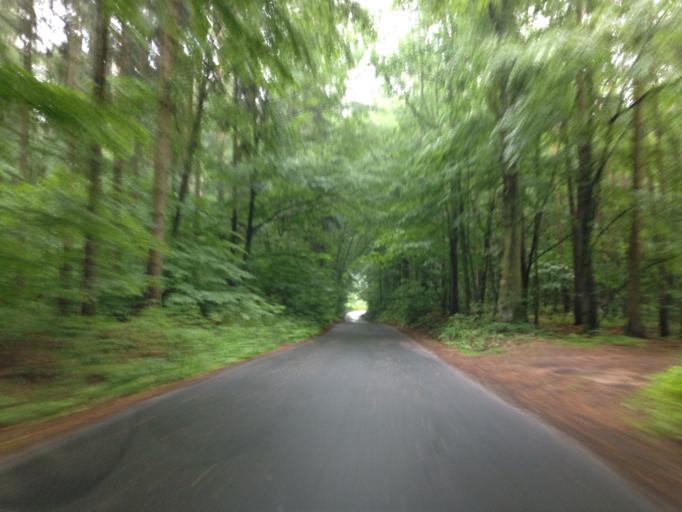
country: PL
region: Kujawsko-Pomorskie
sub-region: Powiat brodnicki
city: Jablonowo Pomorskie
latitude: 53.4467
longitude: 19.1870
